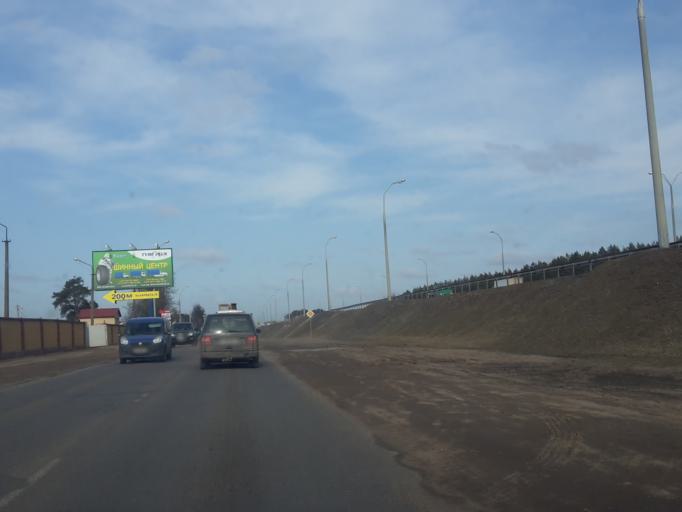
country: BY
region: Minsk
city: Vyaliki Trastsyanets
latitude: 53.9074
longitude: 27.6864
